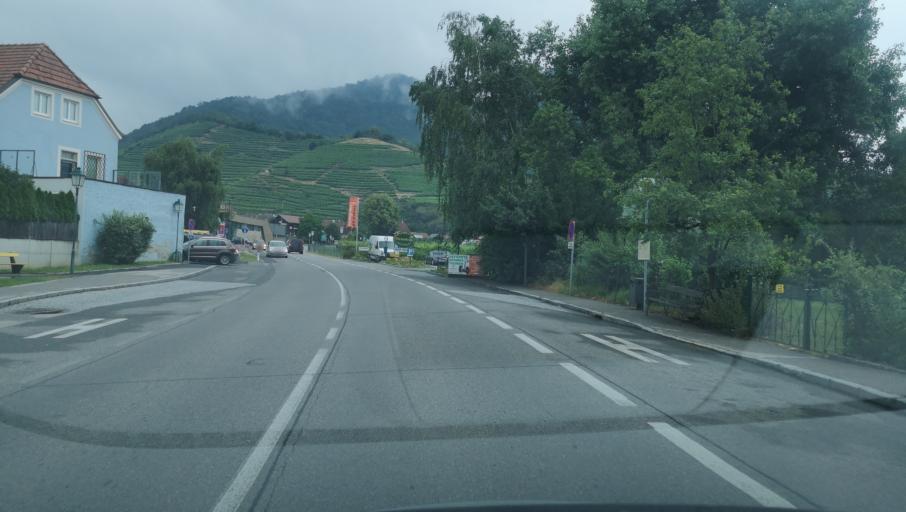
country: AT
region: Lower Austria
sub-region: Politischer Bezirk Krems
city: Spitz
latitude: 48.3631
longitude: 15.4175
